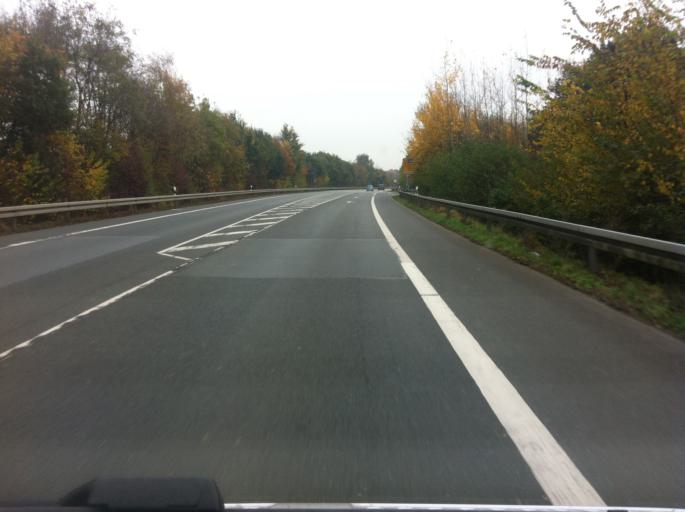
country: DE
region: North Rhine-Westphalia
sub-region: Regierungsbezirk Munster
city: Gescher
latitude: 51.9399
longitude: 7.0274
